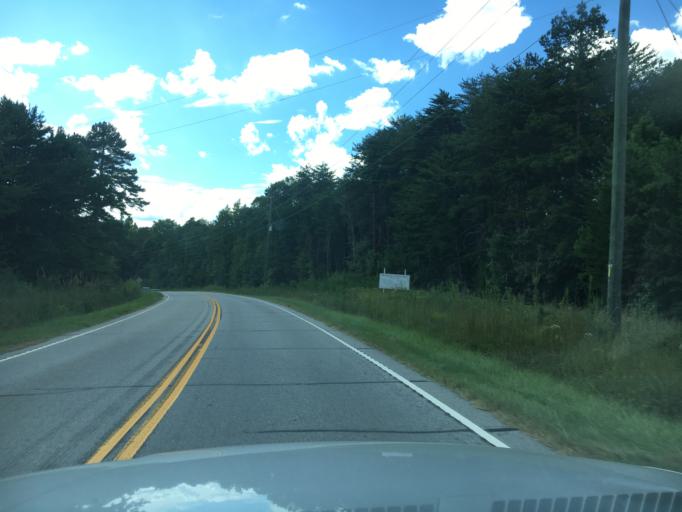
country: US
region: South Carolina
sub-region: Laurens County
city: Laurens
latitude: 34.5229
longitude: -82.1507
